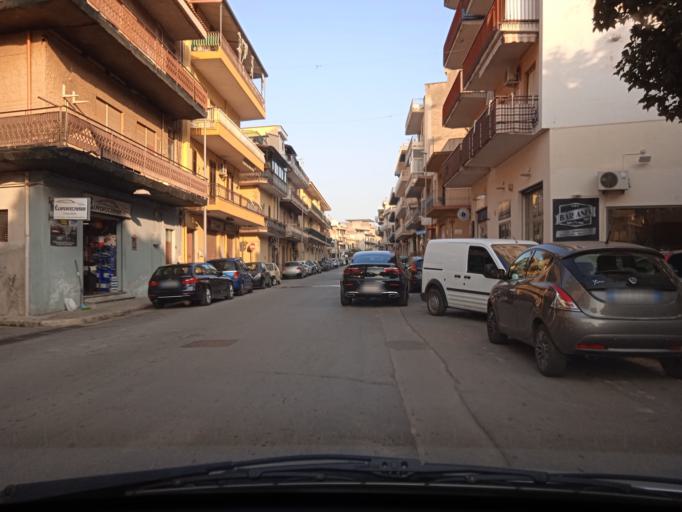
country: IT
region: Sicily
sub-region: Palermo
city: Villabate
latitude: 38.0754
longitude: 13.4473
